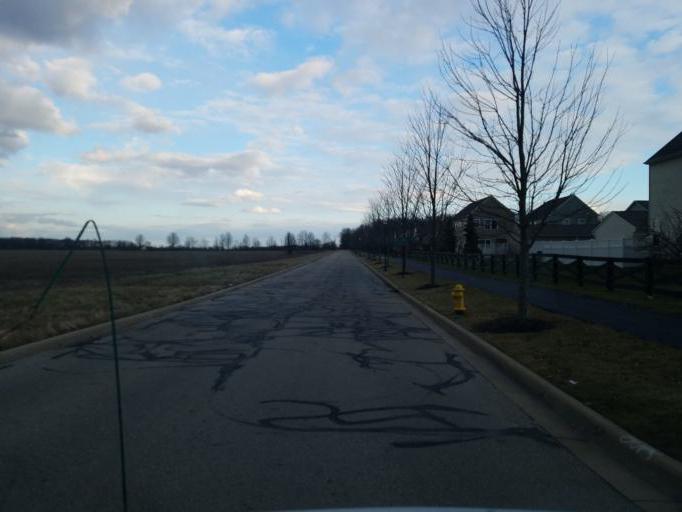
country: US
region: Ohio
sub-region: Delaware County
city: Delaware
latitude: 40.3209
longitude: -83.1078
